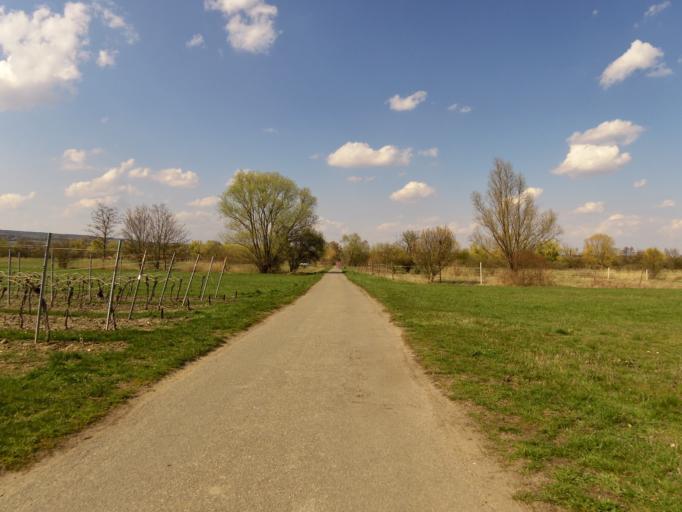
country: DE
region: Rheinland-Pfalz
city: Erpolzheim
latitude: 49.4804
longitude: 8.2045
